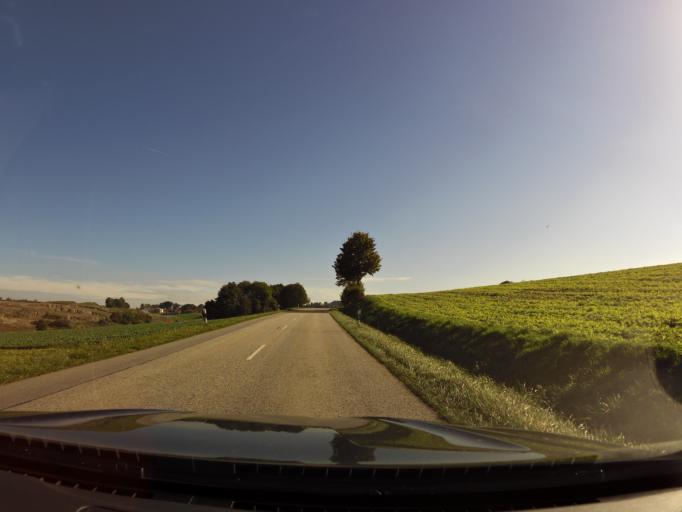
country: DE
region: Bavaria
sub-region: Lower Bavaria
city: Tiefenbach
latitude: 48.4812
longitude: 12.1196
